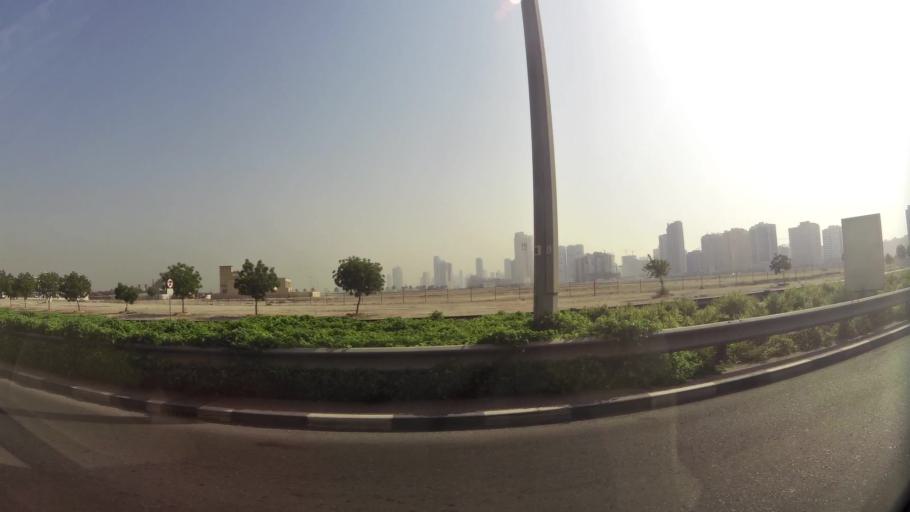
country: AE
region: Ash Shariqah
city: Sharjah
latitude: 25.2910
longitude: 55.3544
